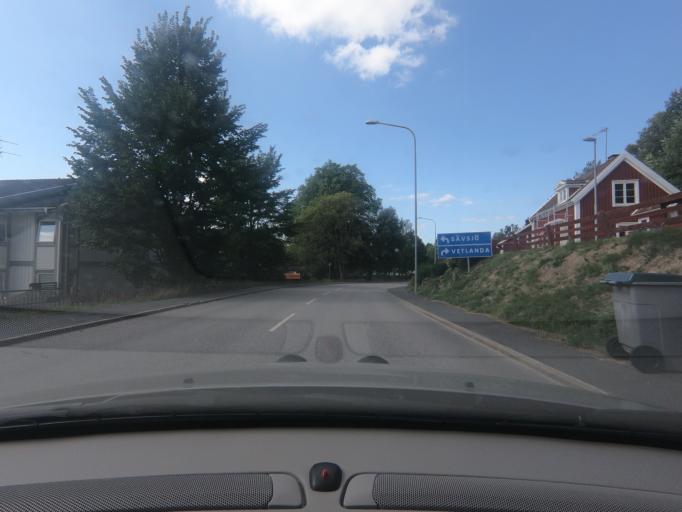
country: SE
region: Joenkoeping
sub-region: Vetlanda Kommun
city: Landsbro
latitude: 57.3685
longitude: 14.9036
